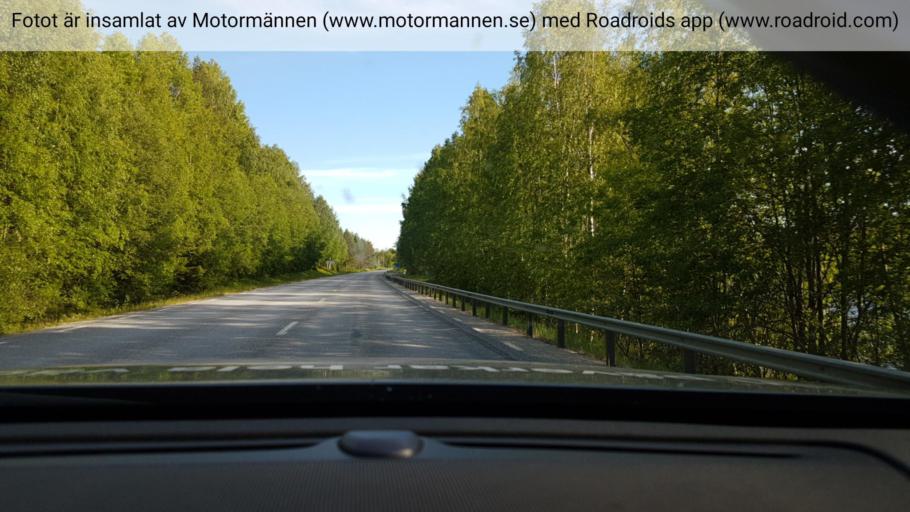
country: SE
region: Vaesterbotten
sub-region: Vindelns Kommun
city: Vindeln
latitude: 64.2990
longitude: 19.6177
